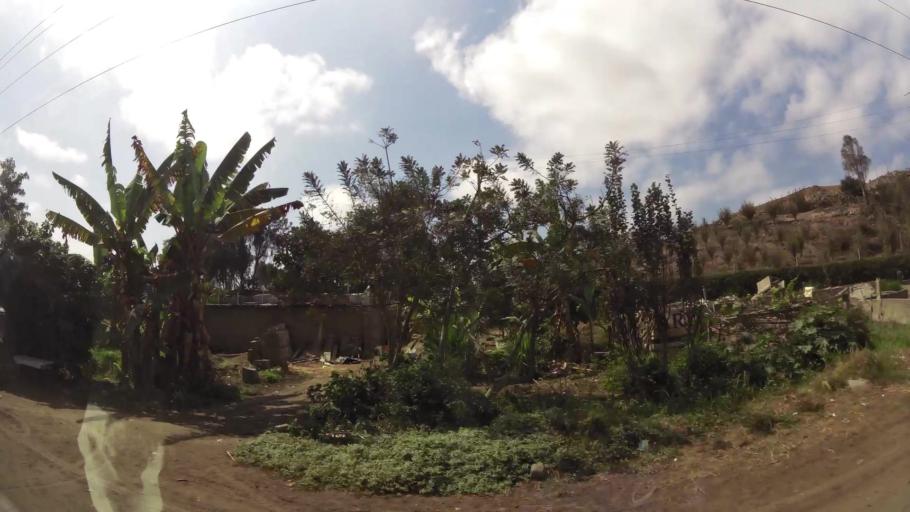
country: PE
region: Lima
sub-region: Provincia de Canete
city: Mala
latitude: -12.6767
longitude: -76.6289
